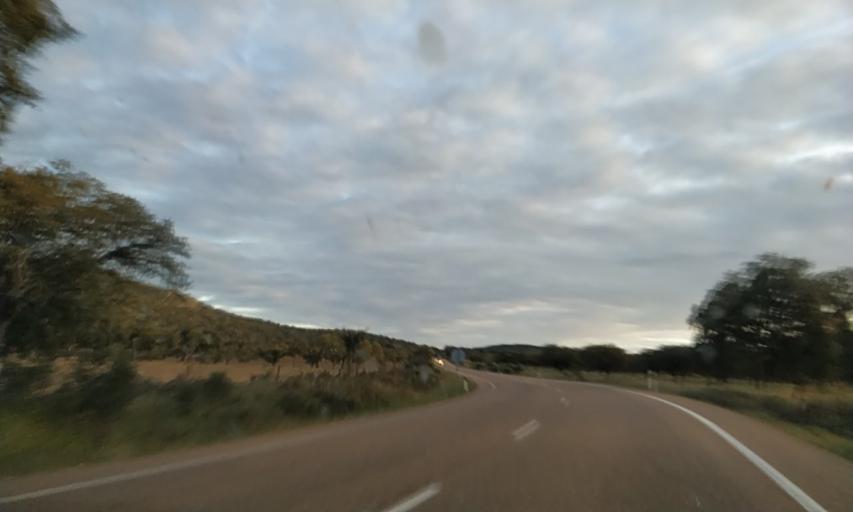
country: ES
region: Extremadura
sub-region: Provincia de Badajoz
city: Puebla de Obando
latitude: 39.2090
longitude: -6.5856
